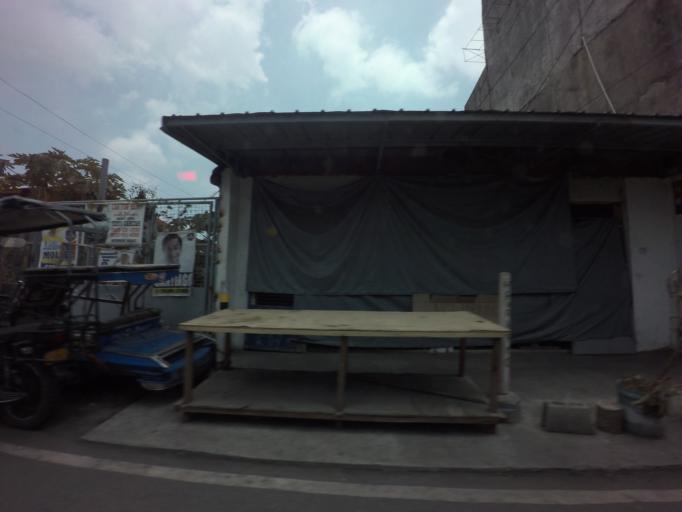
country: PH
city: Sambayanihan People's Village
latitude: 14.4352
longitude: 121.0501
